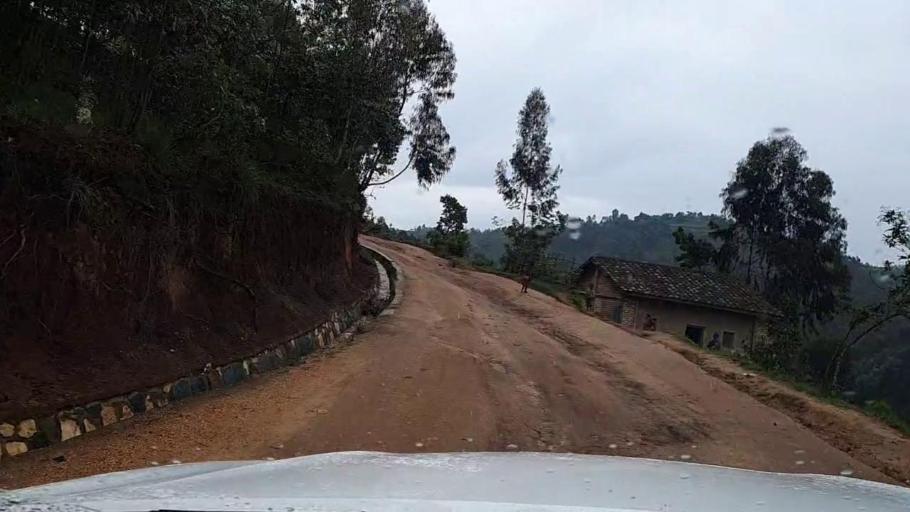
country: RW
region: Southern Province
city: Nzega
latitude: -2.4684
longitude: 29.5041
